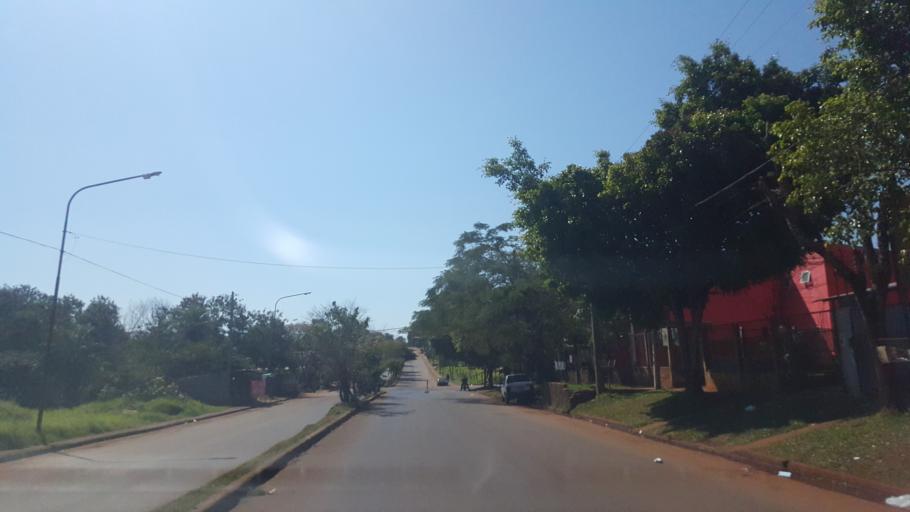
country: AR
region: Misiones
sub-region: Departamento de Capital
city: Posadas
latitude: -27.3872
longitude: -55.9421
